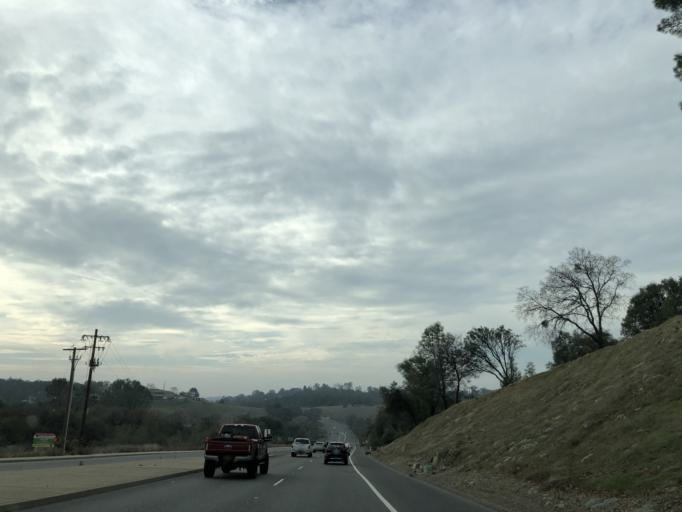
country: US
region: California
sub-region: El Dorado County
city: El Dorado Hills
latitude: 38.7095
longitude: -121.0868
